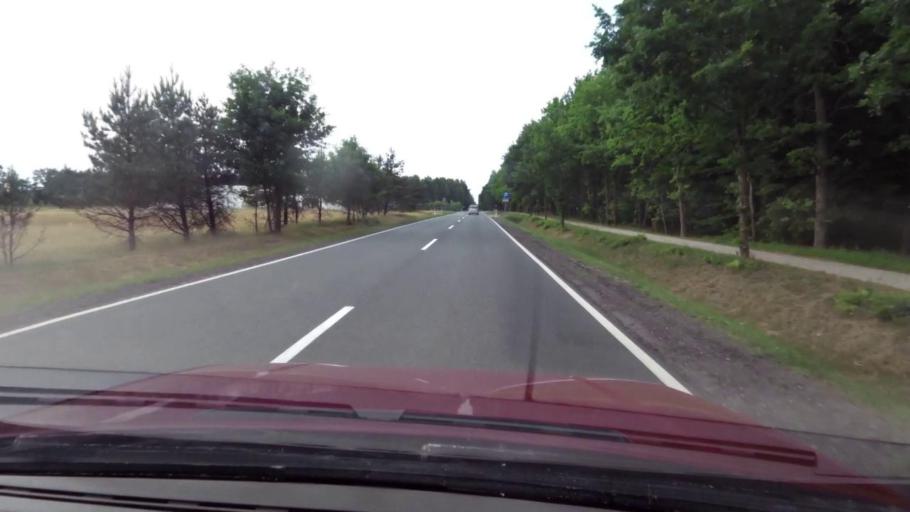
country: PL
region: Pomeranian Voivodeship
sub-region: Powiat bytowski
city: Trzebielino
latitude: 54.2157
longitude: 17.0888
